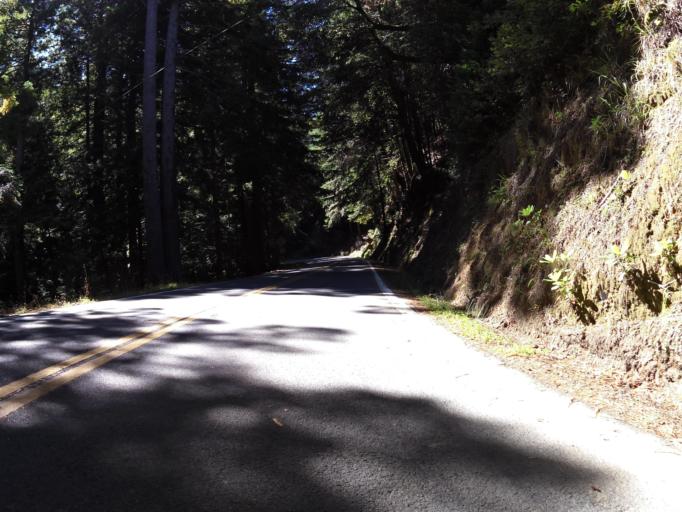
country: US
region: California
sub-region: Mendocino County
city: Fort Bragg
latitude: 39.7247
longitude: -123.8087
